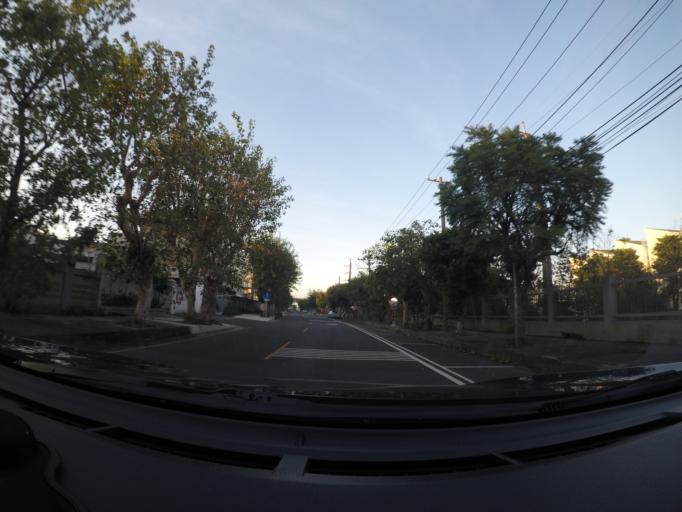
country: TW
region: Taiwan
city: Taoyuan City
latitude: 24.9911
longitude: 121.2463
